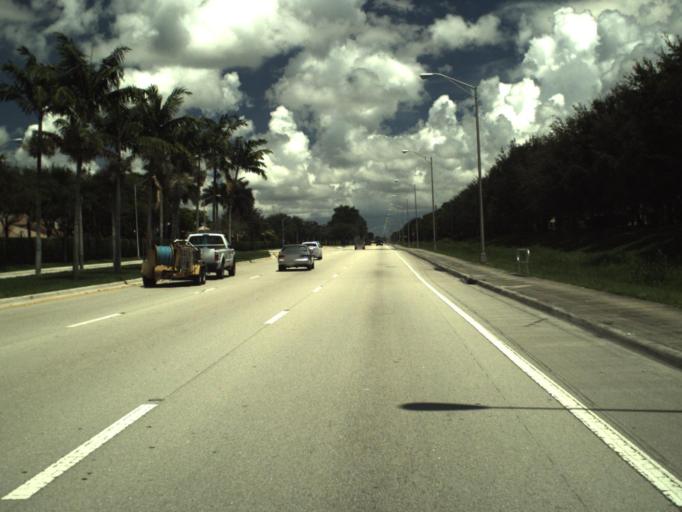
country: US
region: Florida
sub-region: Miami-Dade County
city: Country Club
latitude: 25.9789
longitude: -80.3296
